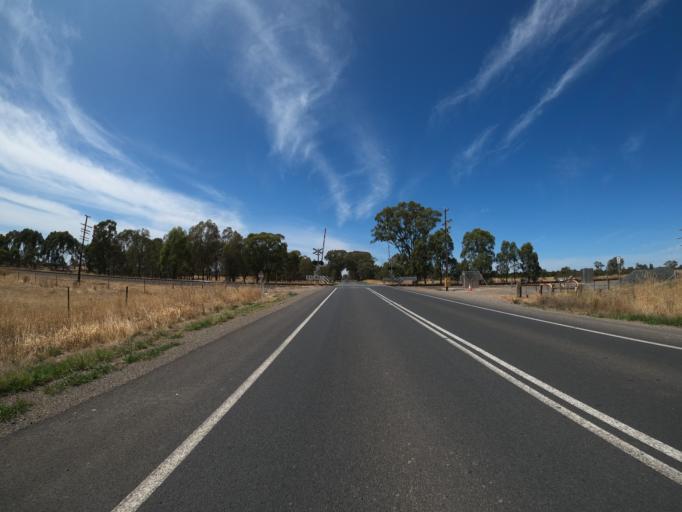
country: AU
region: Victoria
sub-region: Benalla
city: Benalla
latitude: -36.5230
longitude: 146.0365
